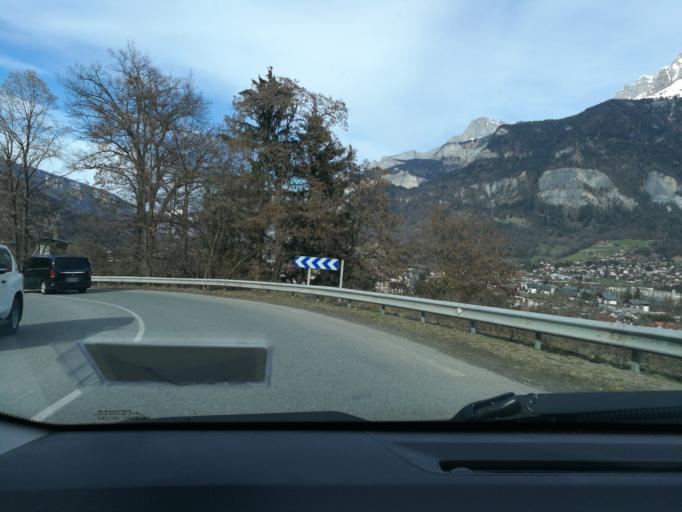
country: FR
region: Rhone-Alpes
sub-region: Departement de la Haute-Savoie
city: Sallanches
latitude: 45.9288
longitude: 6.6320
